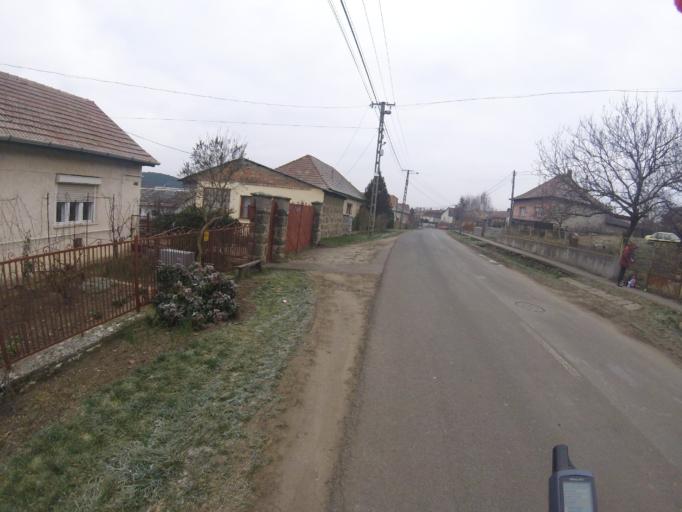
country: HU
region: Nograd
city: Paszto
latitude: 47.9580
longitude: 19.6877
